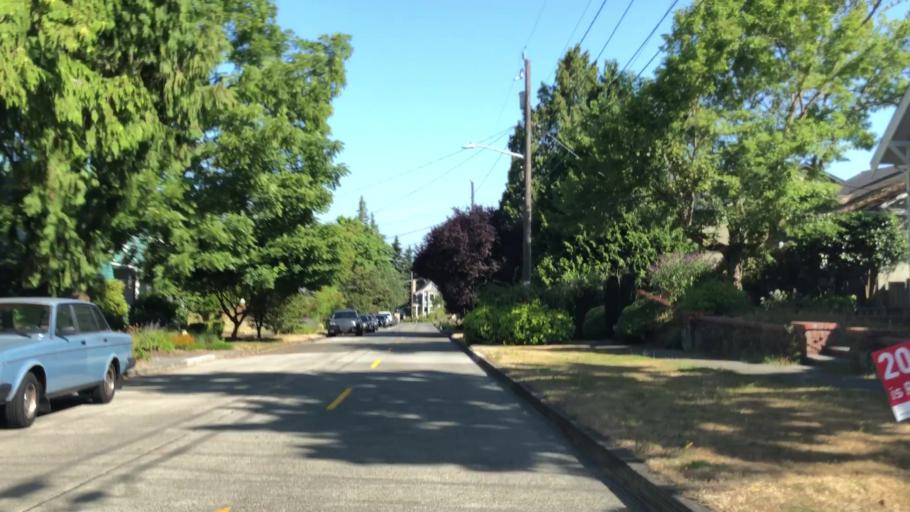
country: US
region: Washington
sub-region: King County
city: Seattle
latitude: 47.6703
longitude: -122.3326
